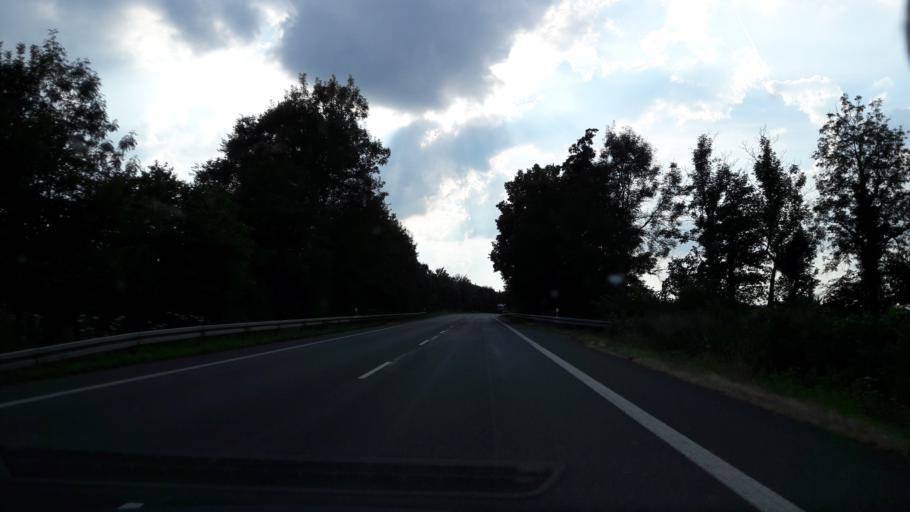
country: DE
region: North Rhine-Westphalia
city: Sendenhorst
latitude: 51.8261
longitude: 7.8894
